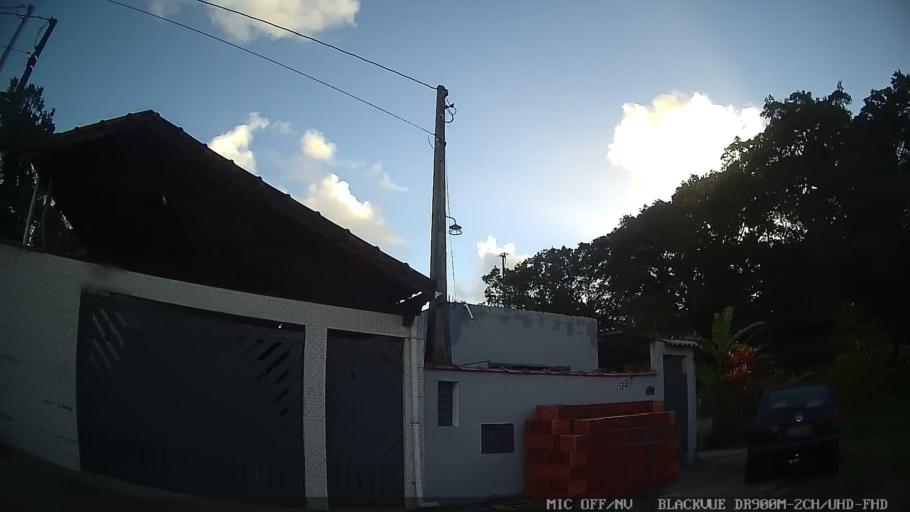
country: BR
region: Sao Paulo
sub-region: Itanhaem
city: Itanhaem
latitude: -24.1405
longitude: -46.7214
